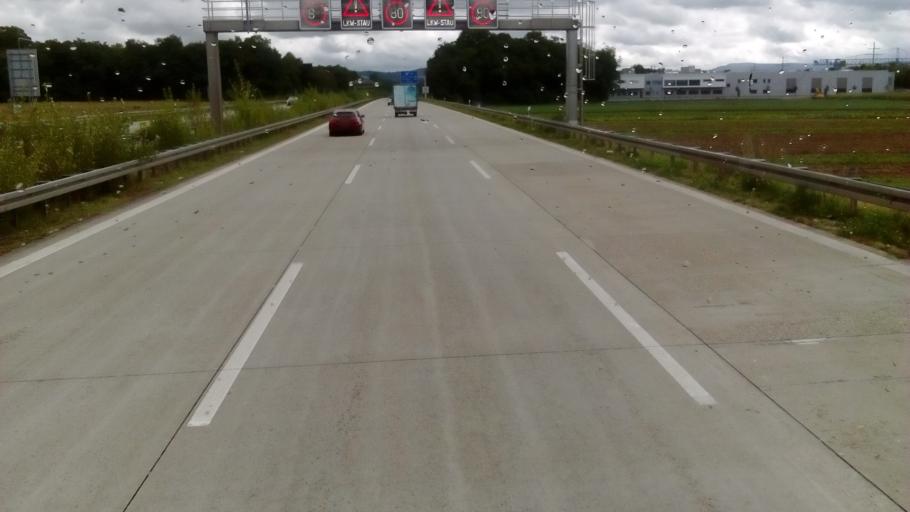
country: FR
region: Alsace
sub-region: Departement du Haut-Rhin
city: Huningue
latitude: 47.6150
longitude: 7.5872
